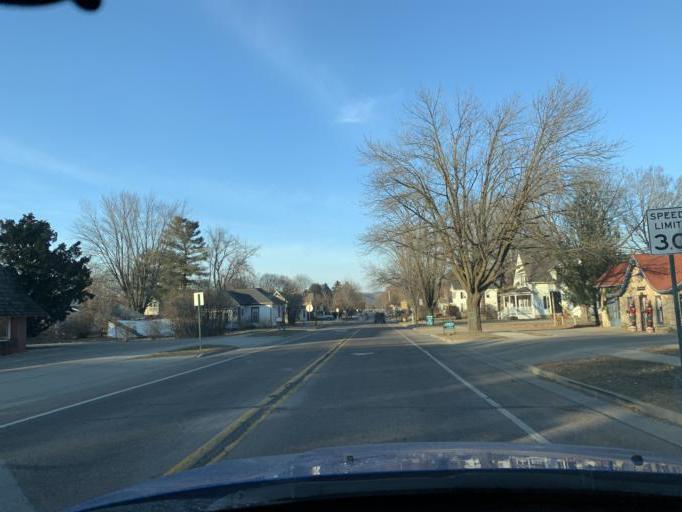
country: US
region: Wisconsin
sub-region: Sauk County
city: Spring Green
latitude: 43.1760
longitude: -90.0640
